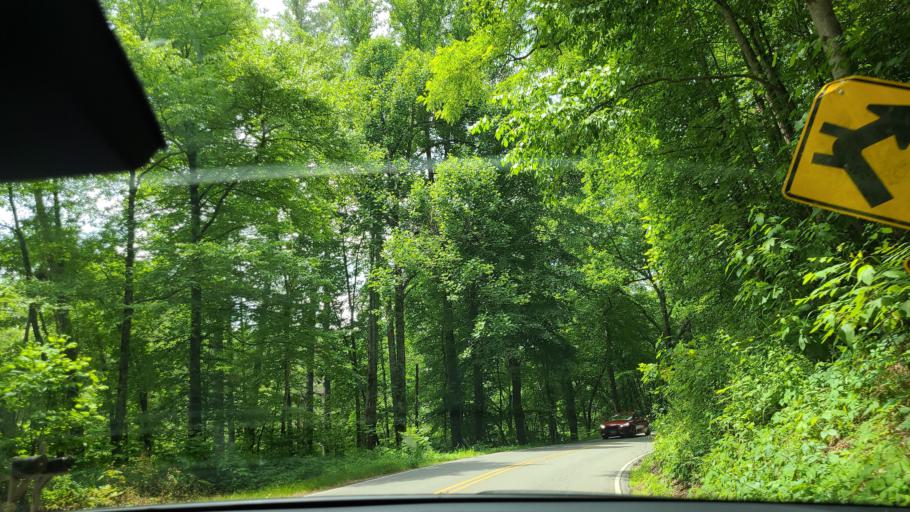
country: US
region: North Carolina
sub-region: Macon County
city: Franklin
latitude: 35.1263
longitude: -83.2807
